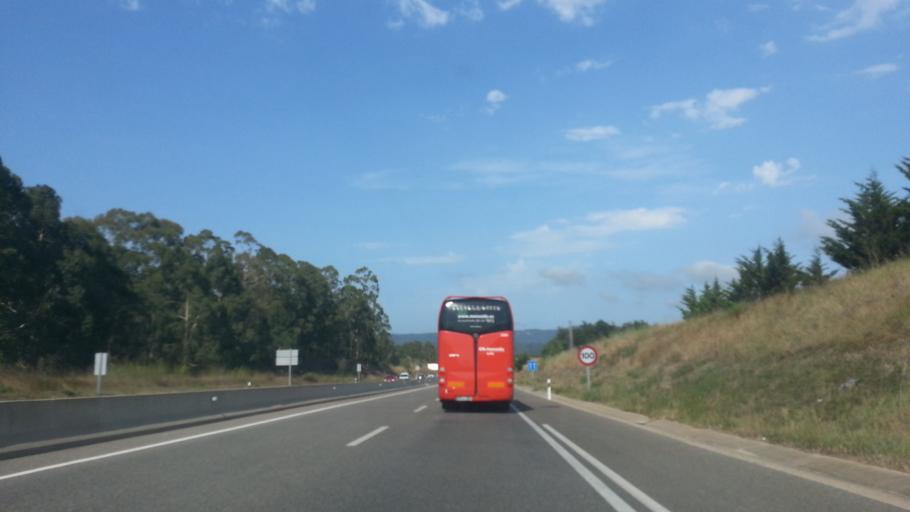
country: ES
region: Catalonia
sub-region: Provincia de Girona
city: Llagostera
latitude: 41.8225
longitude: 2.9106
